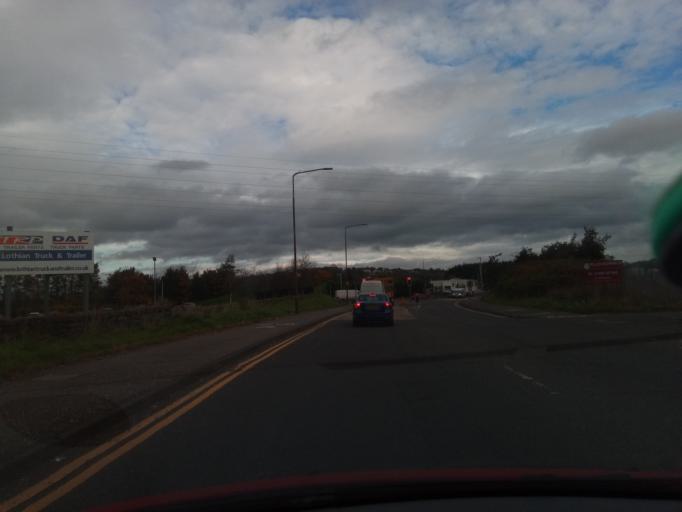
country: GB
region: Scotland
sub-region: West Lothian
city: Blackburn
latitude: 55.8848
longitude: -3.6242
